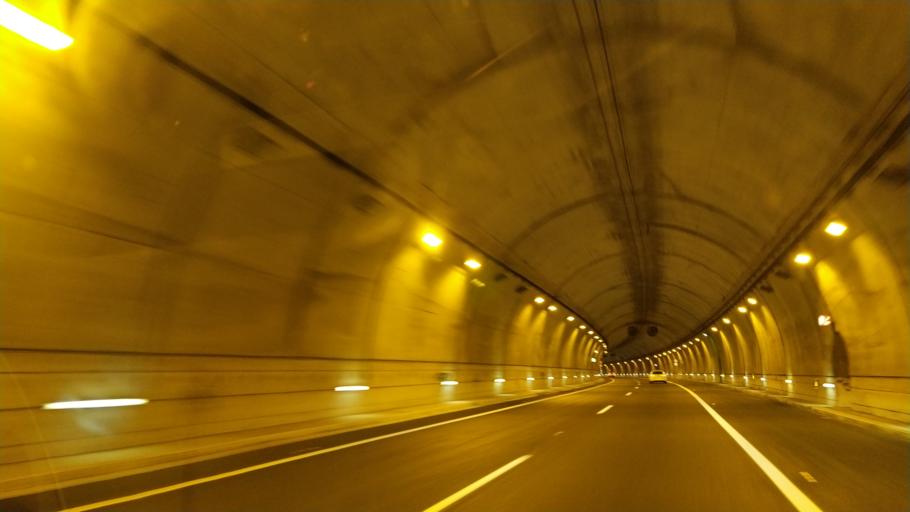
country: ES
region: Cantabria
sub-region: Provincia de Cantabria
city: Camargo
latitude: 43.3936
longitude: -3.8667
